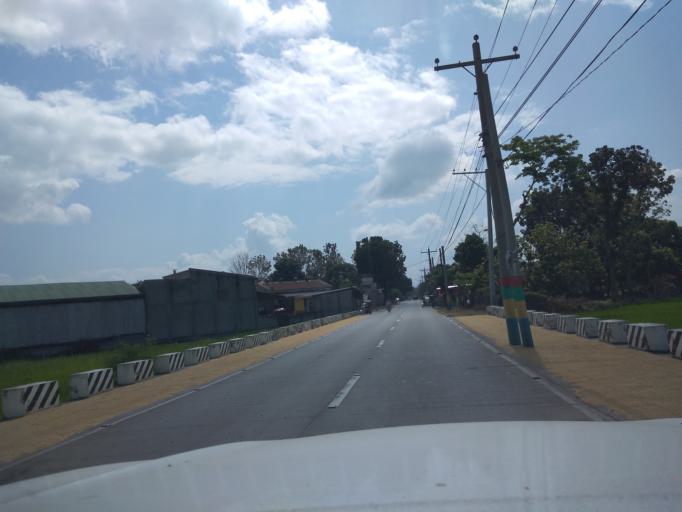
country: PH
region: Central Luzon
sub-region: Province of Pampanga
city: Lourdes
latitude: 15.0223
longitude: 120.8467
